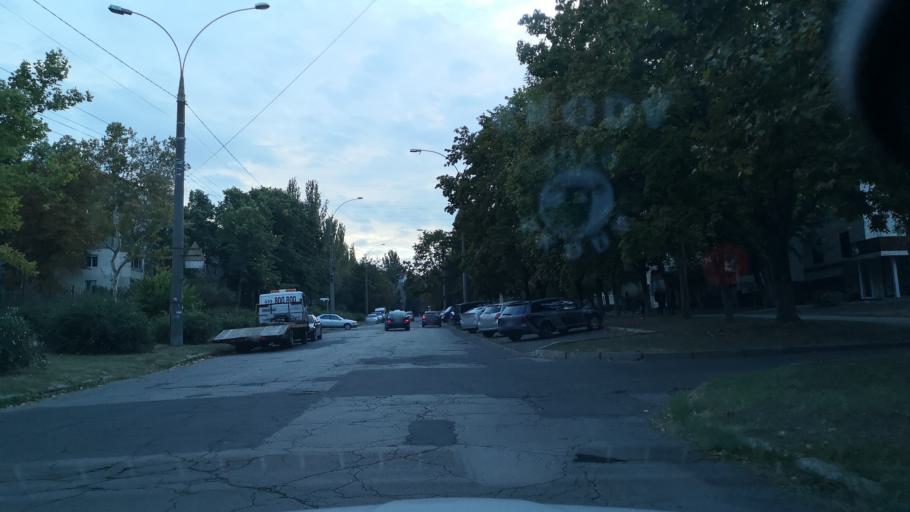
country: MD
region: Chisinau
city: Chisinau
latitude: 46.9863
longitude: 28.8495
